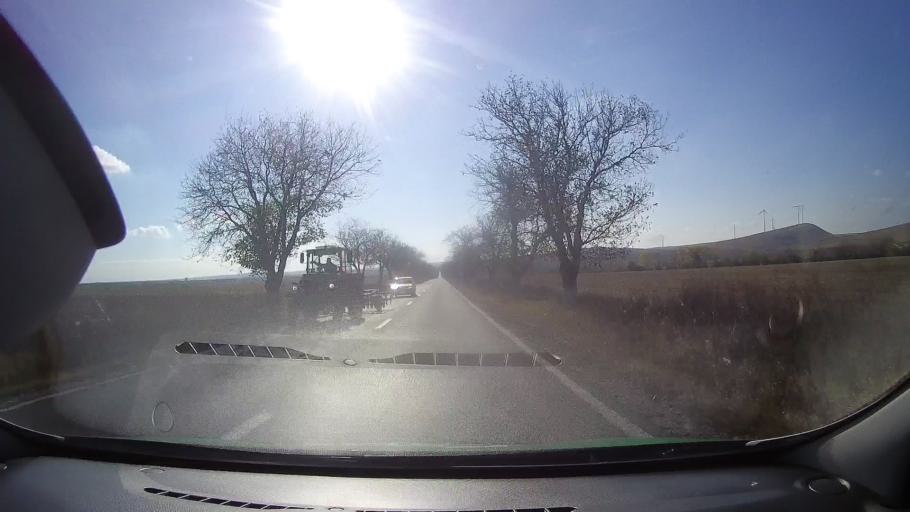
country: RO
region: Tulcea
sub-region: Comuna Ceamurlia de Jos
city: Ceamurlia de Jos
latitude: 44.7819
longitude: 28.6892
